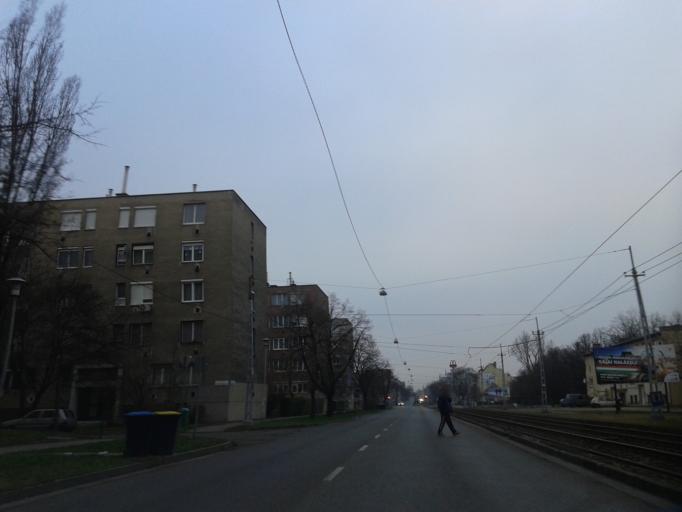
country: HU
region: Budapest
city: Budapest XIV. keruelet
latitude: 47.5133
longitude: 19.1223
